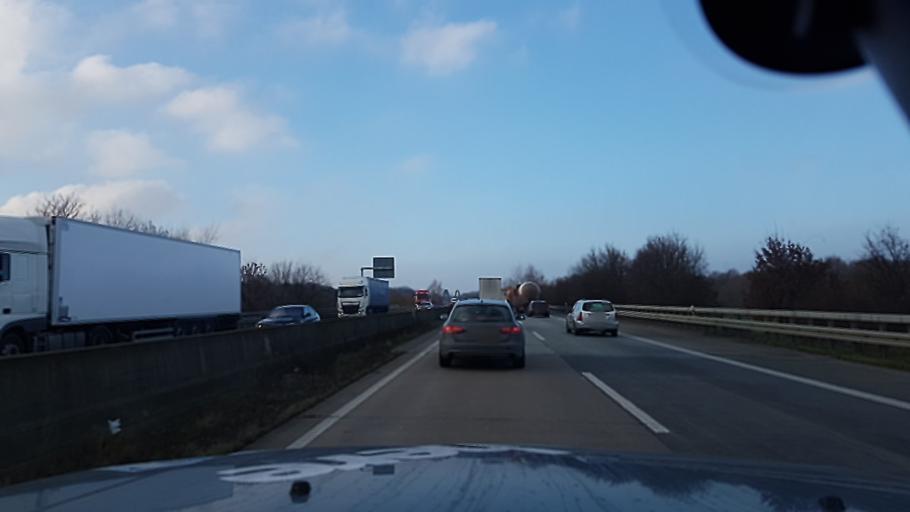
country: DE
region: North Rhine-Westphalia
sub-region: Regierungsbezirk Munster
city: Dreierwalde
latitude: 52.3092
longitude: 7.4780
